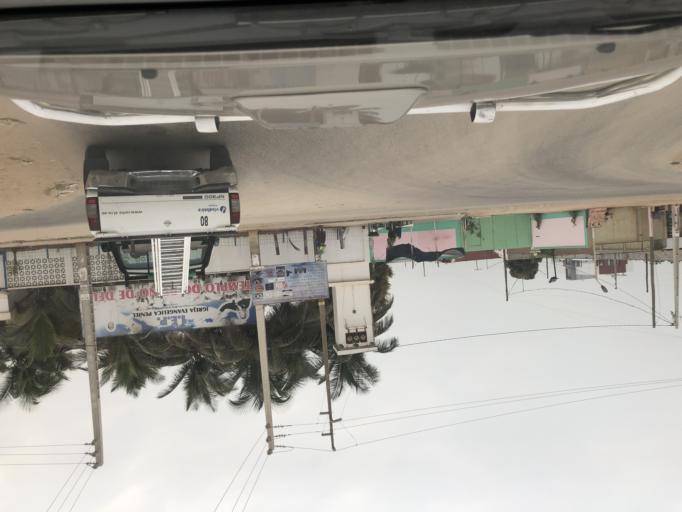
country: AO
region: Luanda
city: Luanda
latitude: -8.8878
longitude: 13.1898
